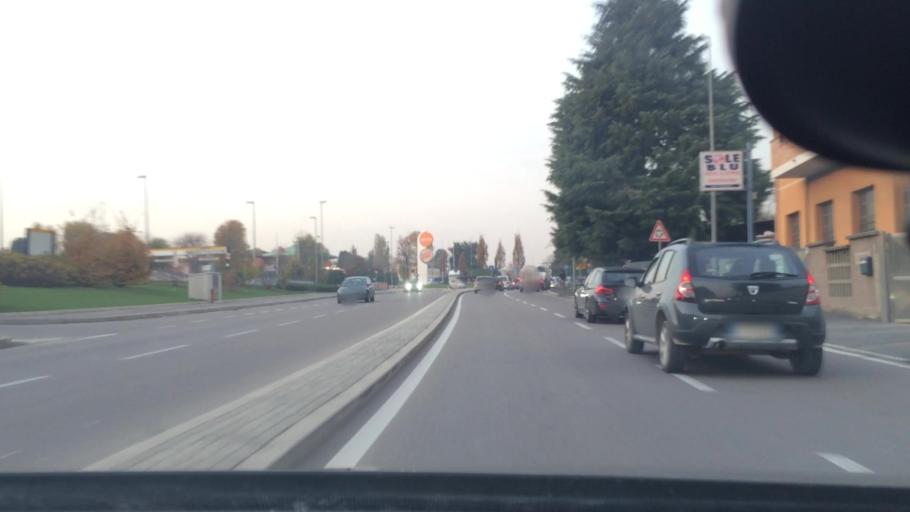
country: IT
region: Lombardy
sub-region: Provincia di Varese
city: Uboldo
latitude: 45.6212
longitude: 9.0192
